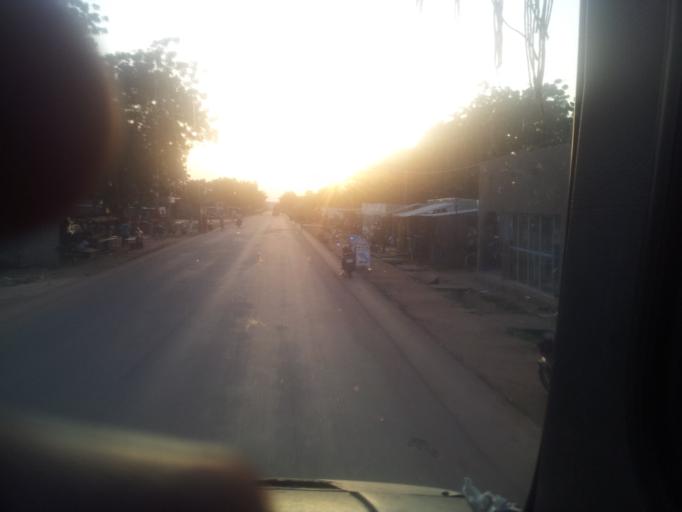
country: BF
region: Centre-Est
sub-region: Kouritenga Province
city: Koupela
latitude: 12.1825
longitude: -0.3555
